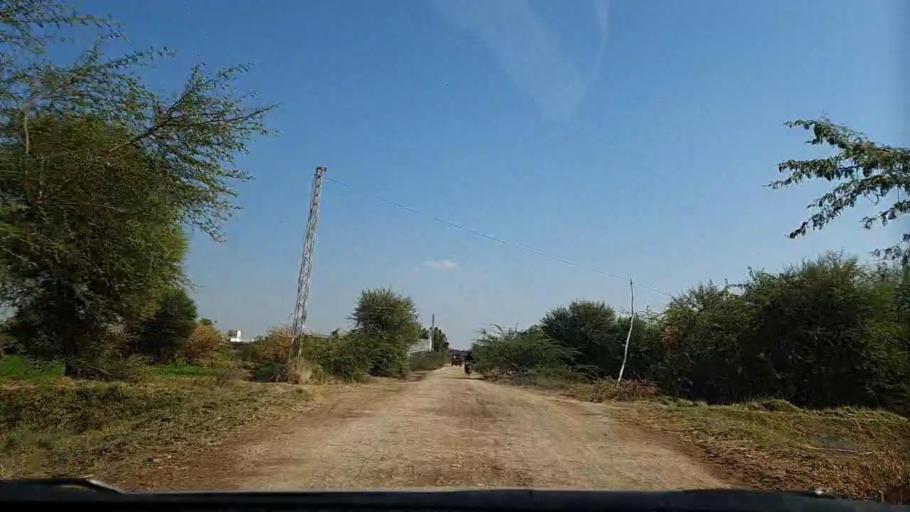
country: PK
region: Sindh
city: Pithoro
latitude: 25.6959
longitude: 69.3545
